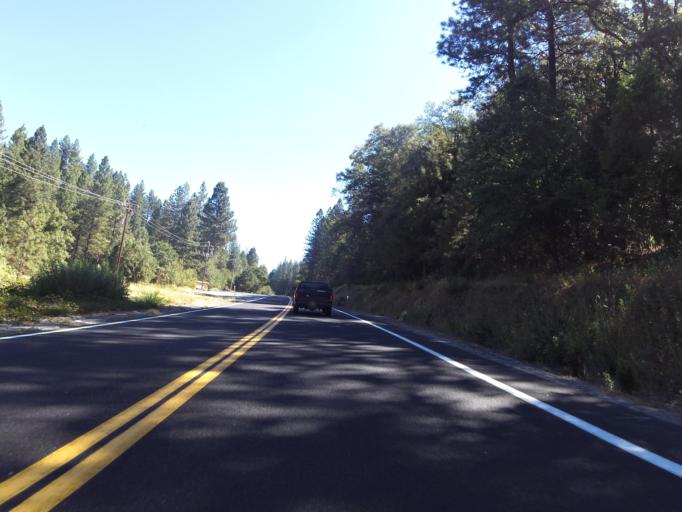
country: US
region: California
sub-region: Calaveras County
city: Forest Meadows
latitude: 38.1653
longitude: -120.4216
